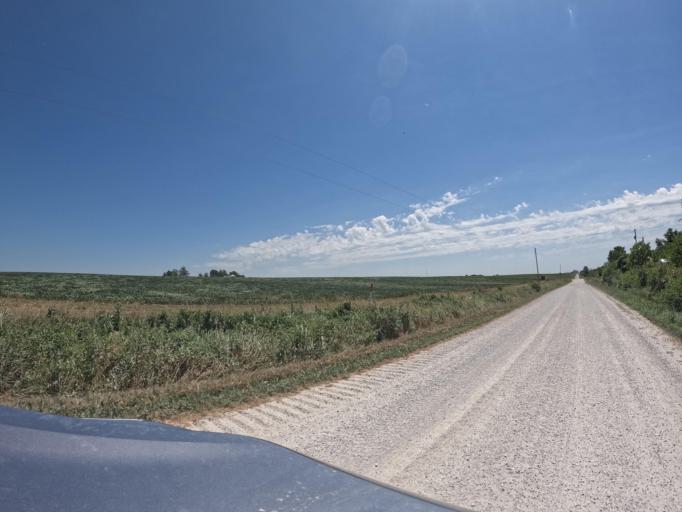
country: US
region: Iowa
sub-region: Keokuk County
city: Sigourney
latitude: 41.4107
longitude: -92.3163
